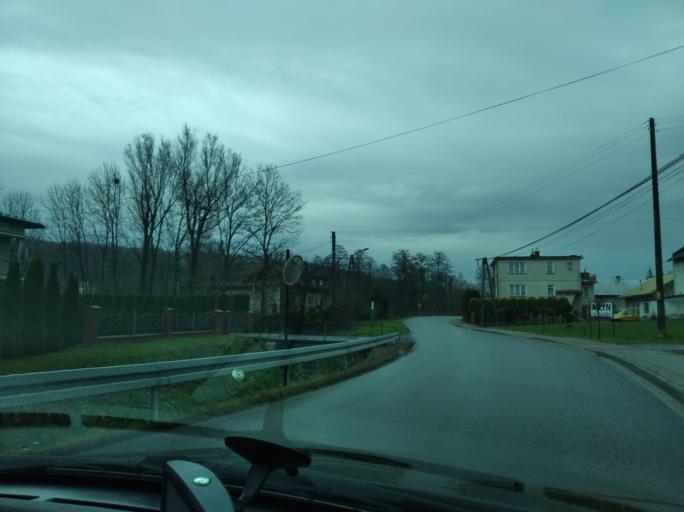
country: PL
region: Subcarpathian Voivodeship
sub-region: Powiat rzeszowski
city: Straszydle
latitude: 49.9187
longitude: 21.9565
